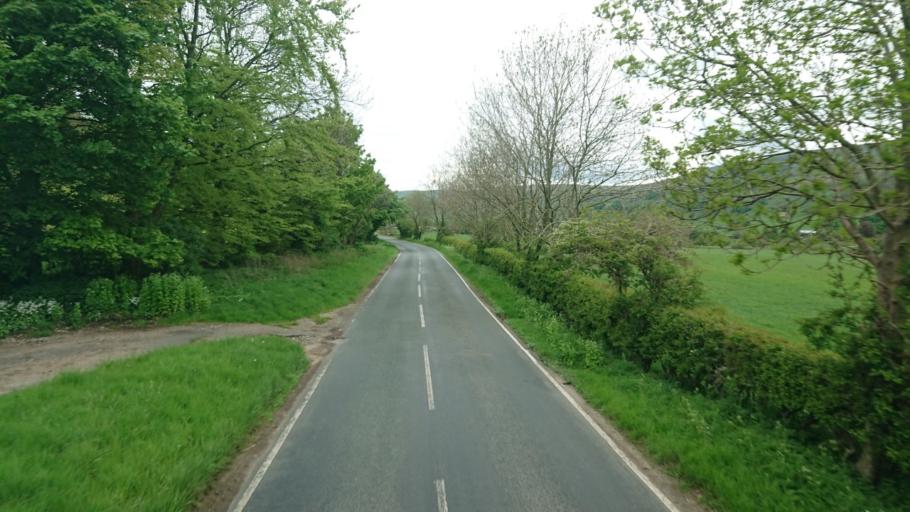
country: GB
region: England
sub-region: North Yorkshire
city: Leyburn
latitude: 54.2590
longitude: -2.0272
